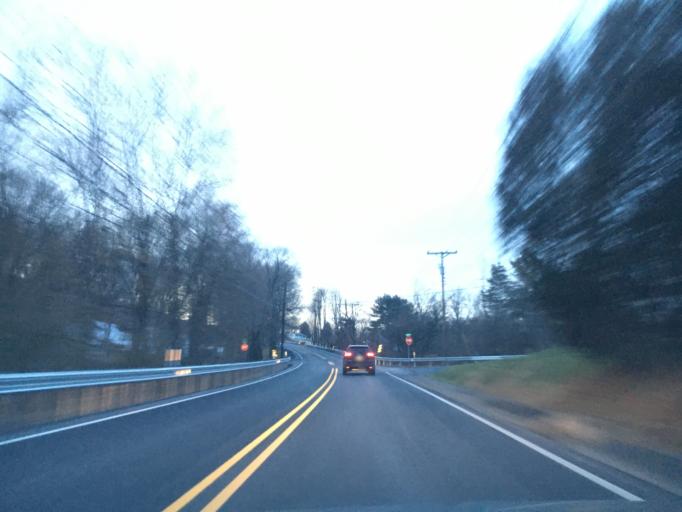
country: US
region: Pennsylvania
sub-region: Northampton County
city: Youngsville
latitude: 40.7517
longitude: -75.4798
